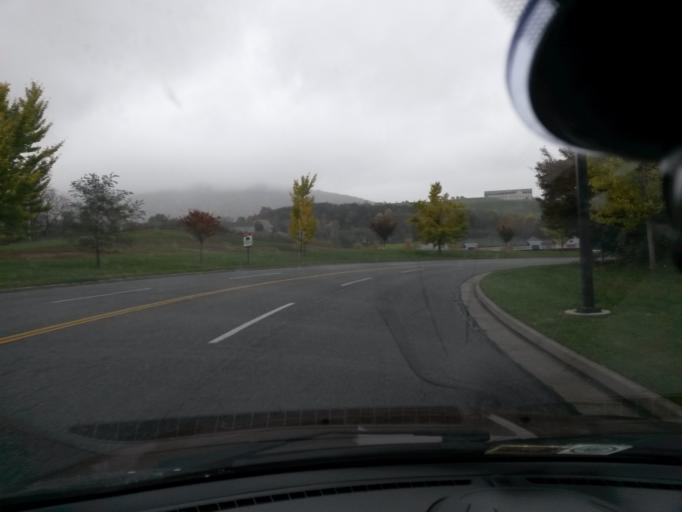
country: US
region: Virginia
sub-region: Roanoke County
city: Vinton
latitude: 37.3095
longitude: -79.8900
